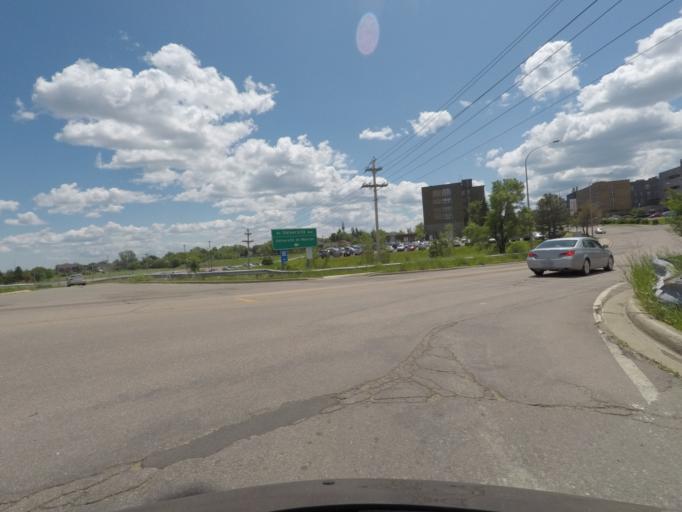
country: CA
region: New Brunswick
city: Moncton
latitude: 46.0998
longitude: -64.7861
